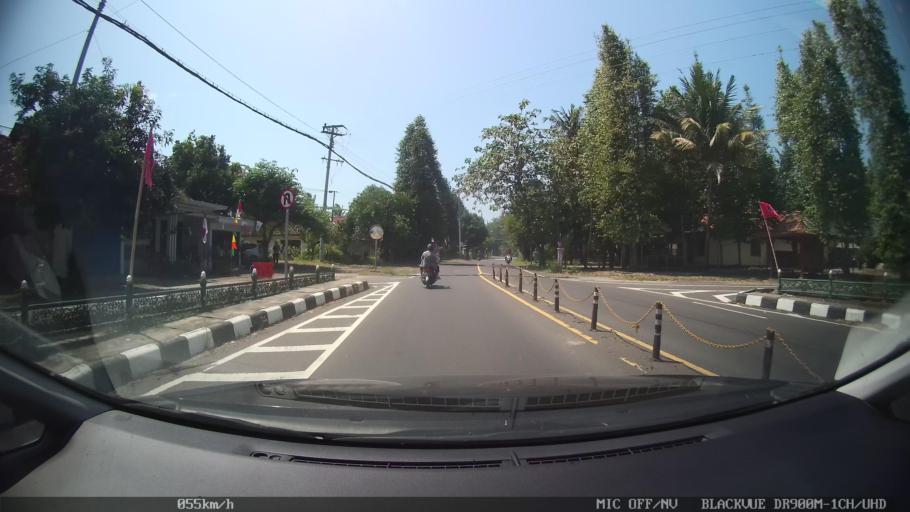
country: ID
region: Daerah Istimewa Yogyakarta
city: Srandakan
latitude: -7.8996
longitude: 110.0659
